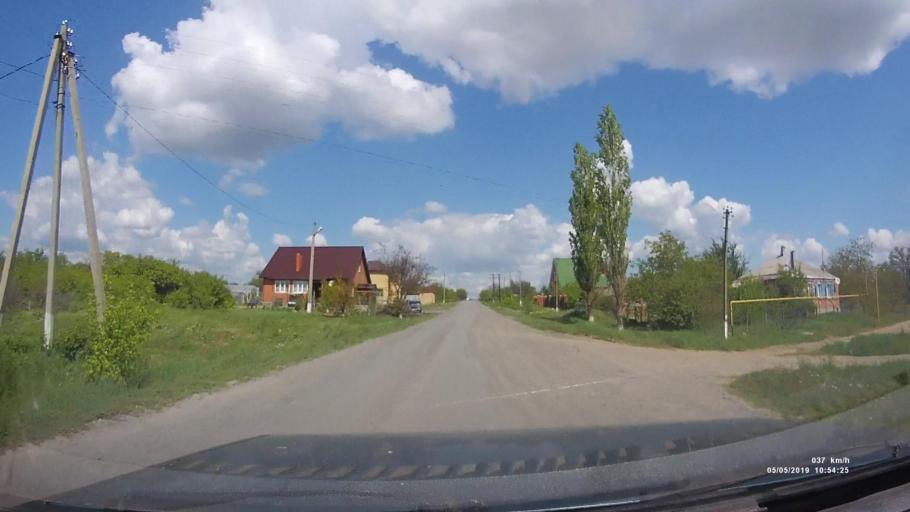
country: RU
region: Rostov
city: Ust'-Donetskiy
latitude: 47.6582
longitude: 40.8231
